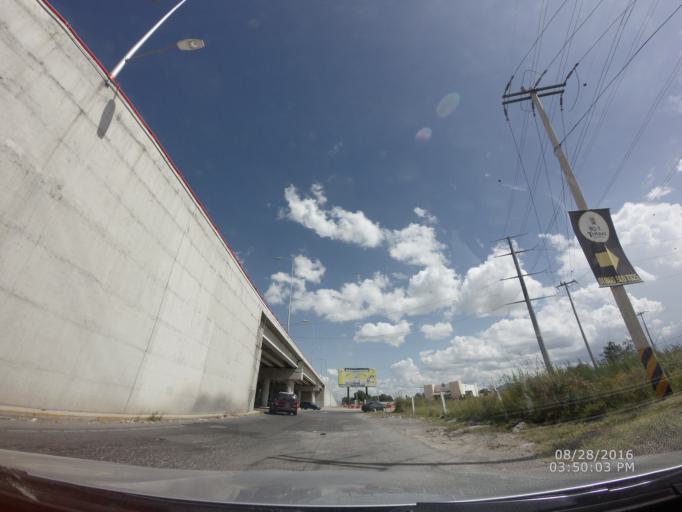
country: MX
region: Hidalgo
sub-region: Mineral de la Reforma
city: Rinconada de los Angeles
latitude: 20.0379
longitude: -98.7320
